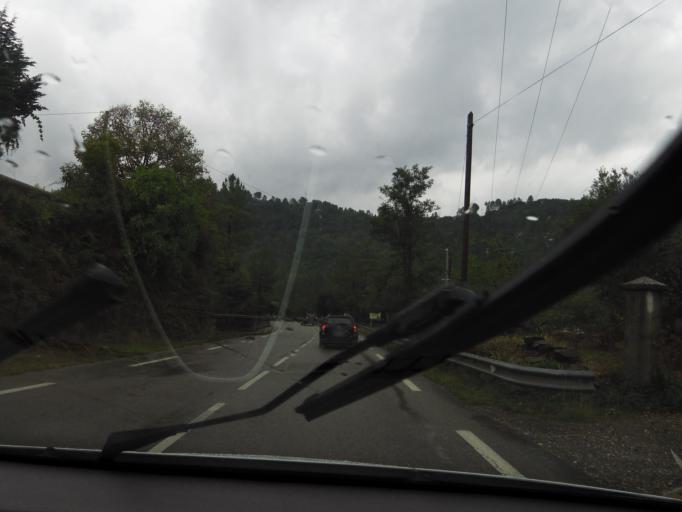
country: FR
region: Languedoc-Roussillon
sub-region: Departement du Gard
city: Branoux-les-Taillades
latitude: 44.2310
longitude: 3.9949
